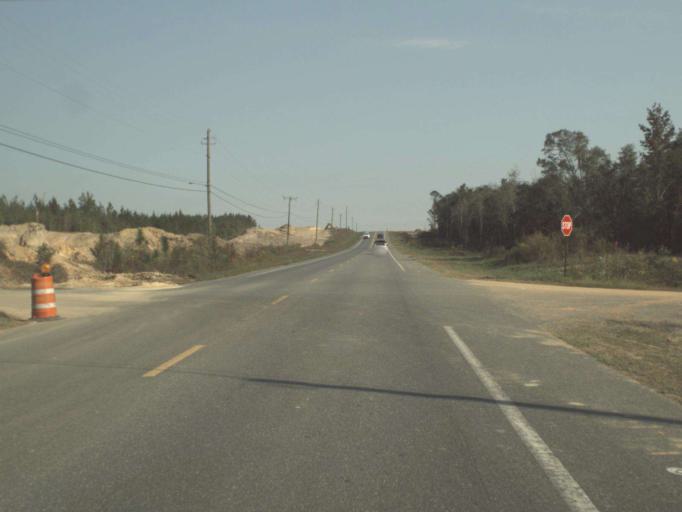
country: US
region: Florida
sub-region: Holmes County
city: Bonifay
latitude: 30.6864
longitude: -85.6864
